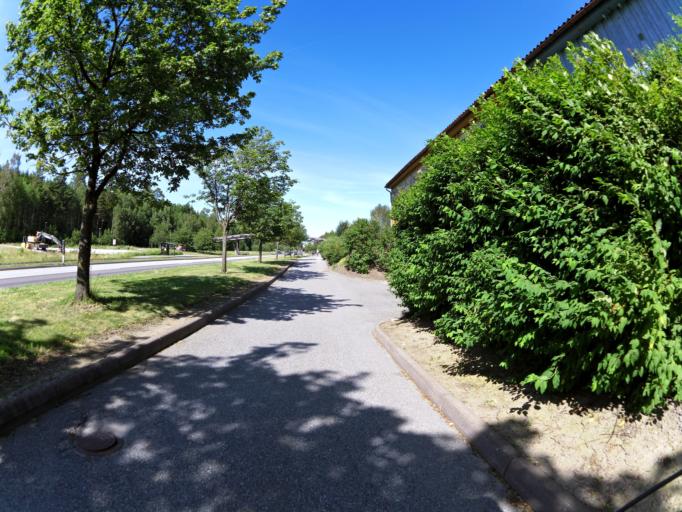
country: NO
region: Ostfold
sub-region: Fredrikstad
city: Fredrikstad
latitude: 59.2292
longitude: 10.9578
